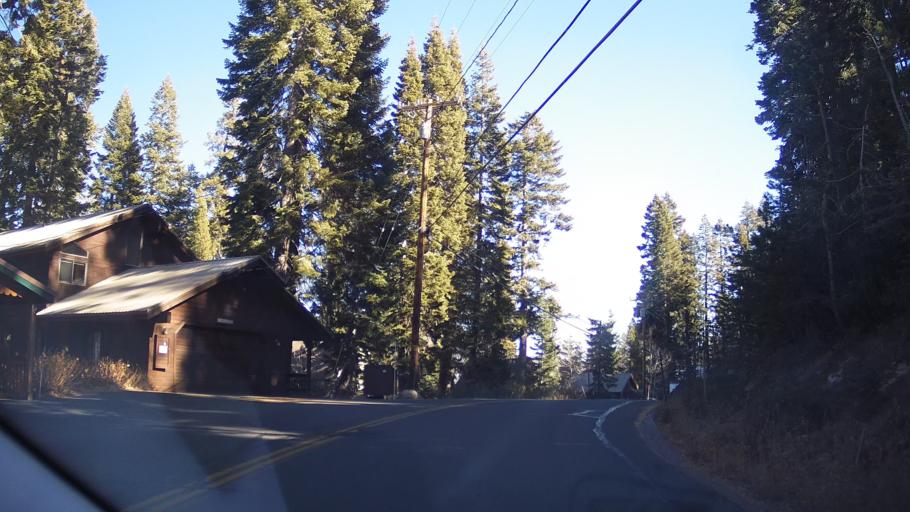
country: US
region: California
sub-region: Nevada County
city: Truckee
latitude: 39.3164
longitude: -120.2813
